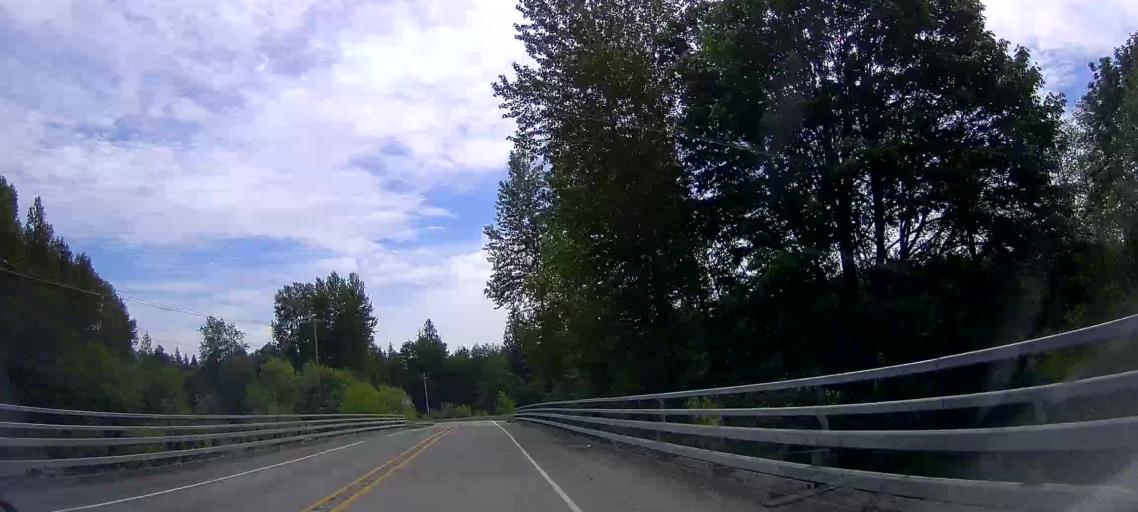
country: US
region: Washington
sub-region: Snohomish County
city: Bryant
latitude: 48.2389
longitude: -122.2052
